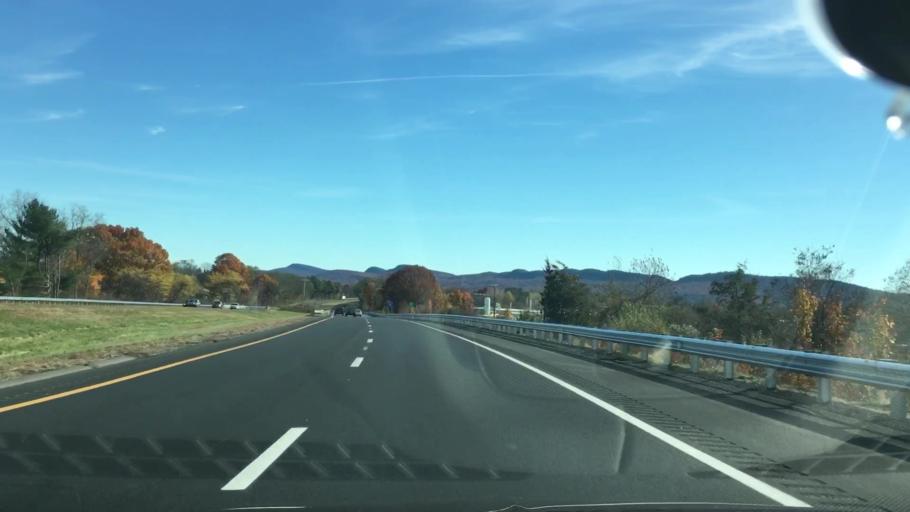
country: US
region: Massachusetts
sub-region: Hampshire County
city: Northampton
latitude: 42.3396
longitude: -72.6368
